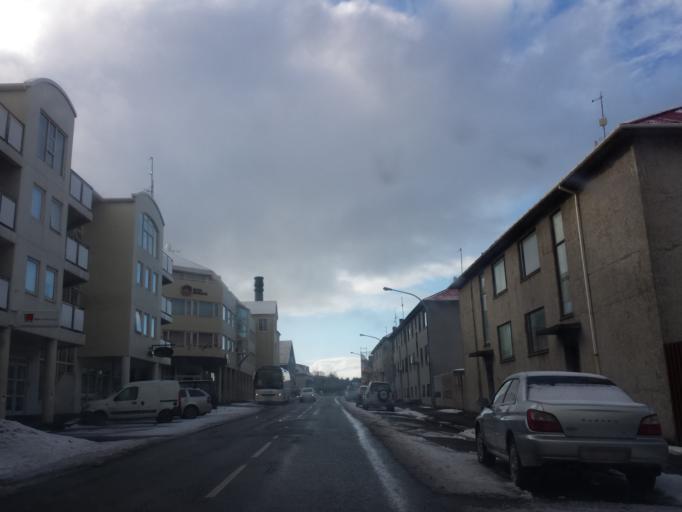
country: IS
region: Capital Region
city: Reykjavik
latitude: 64.1411
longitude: -21.9148
